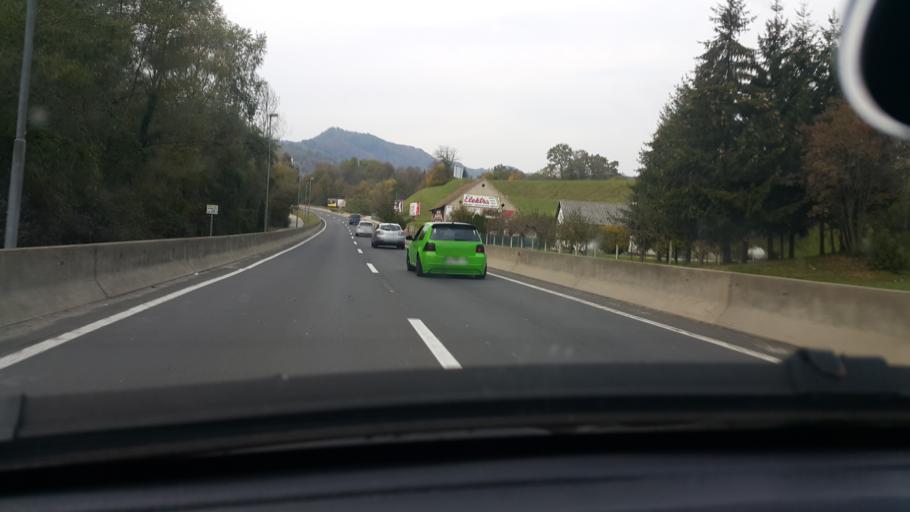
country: SI
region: Maribor
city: Kamnica
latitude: 46.5685
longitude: 15.6199
